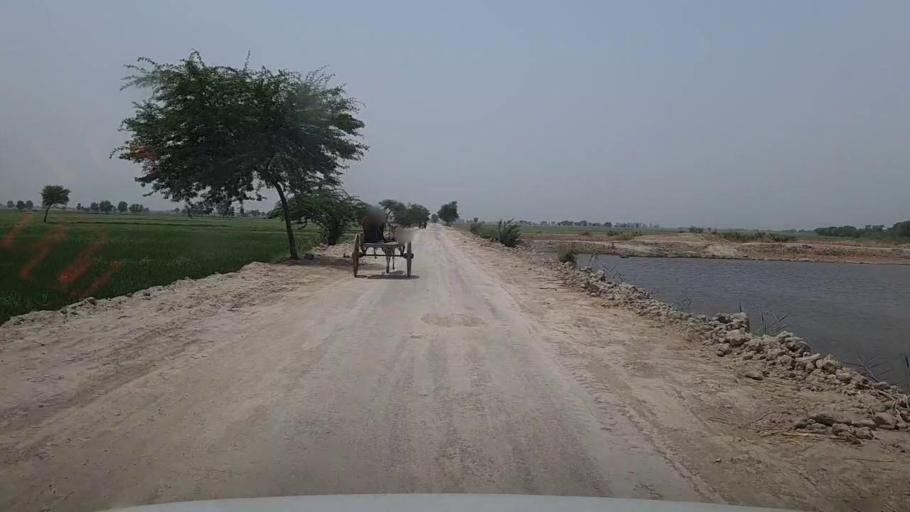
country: PK
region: Sindh
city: Sita Road
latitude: 27.0904
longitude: 67.9141
